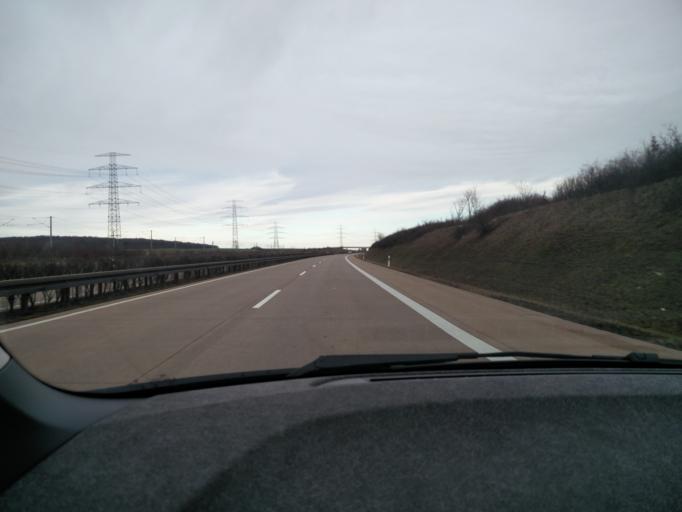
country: DE
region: Thuringia
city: Behringen
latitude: 50.8027
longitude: 10.9991
